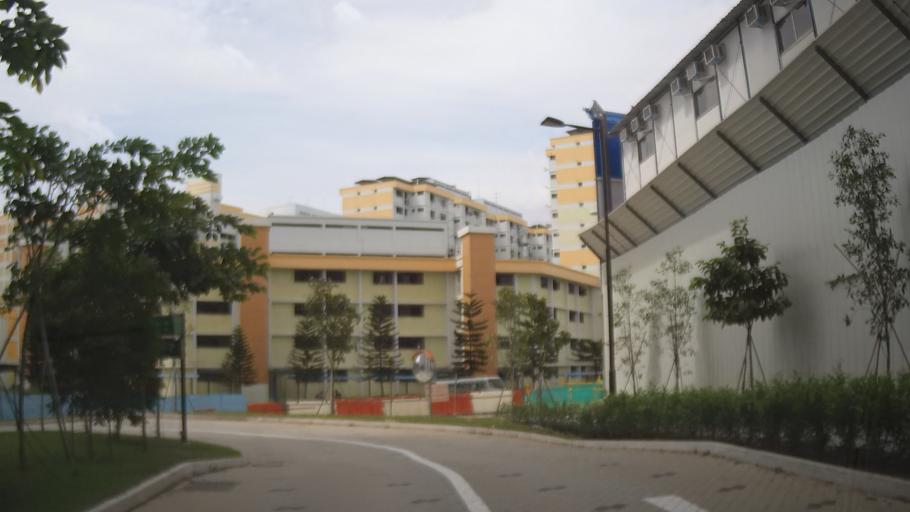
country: MY
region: Johor
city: Johor Bahru
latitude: 1.4364
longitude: 103.7756
